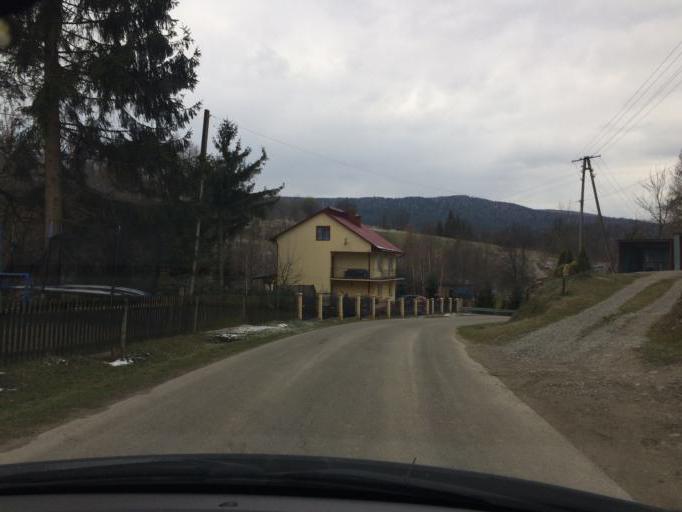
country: PL
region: Subcarpathian Voivodeship
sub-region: Powiat jasielski
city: Nowy Zmigrod
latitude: 49.5802
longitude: 21.4813
